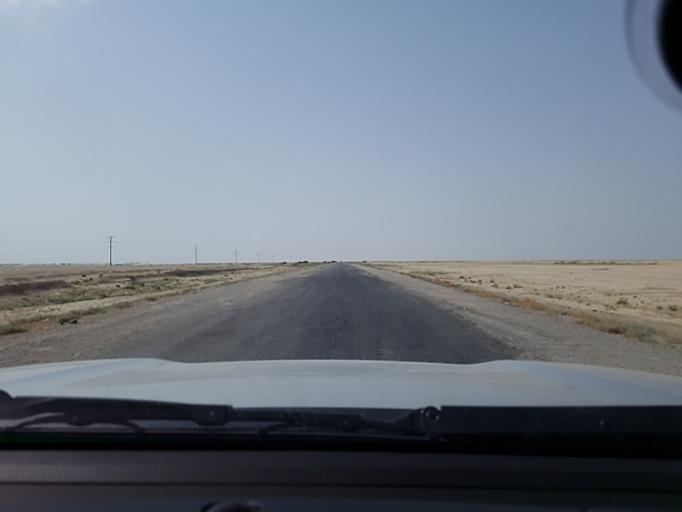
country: TM
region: Balkan
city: Gumdag
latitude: 38.8891
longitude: 54.5930
